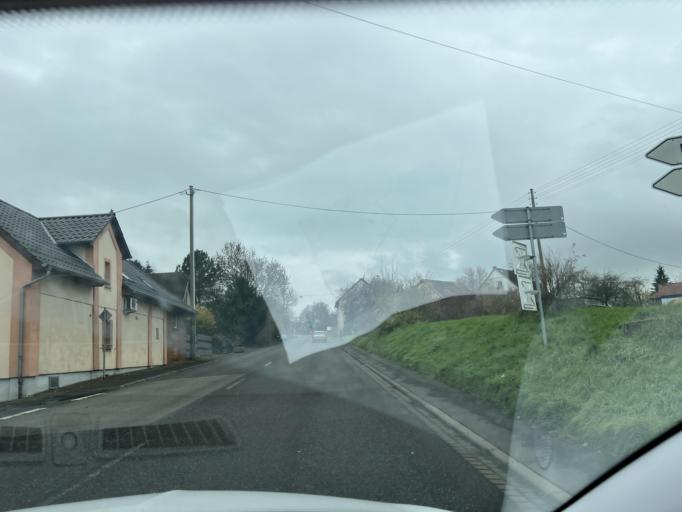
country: GB
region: England
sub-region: Cornwall
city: Tintagel
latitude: 50.9196
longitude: -4.8006
